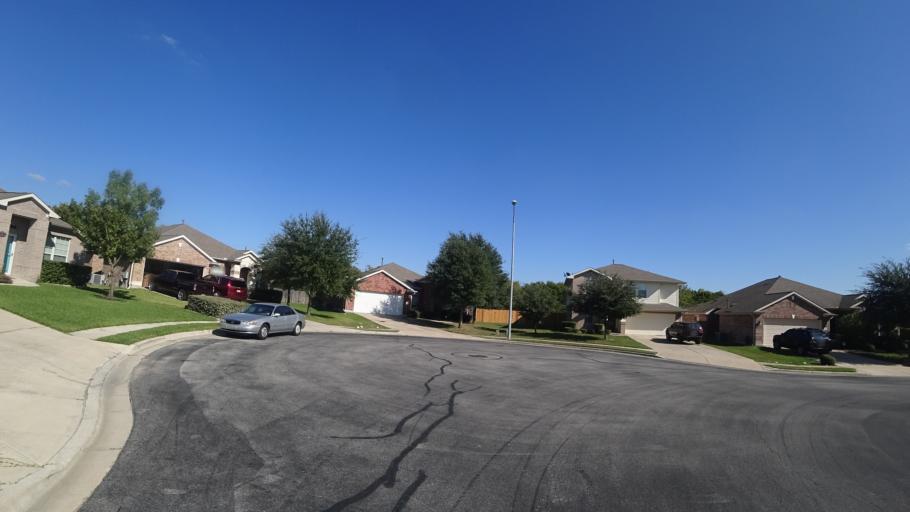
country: US
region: Texas
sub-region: Travis County
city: Manor
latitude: 30.3568
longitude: -97.6083
